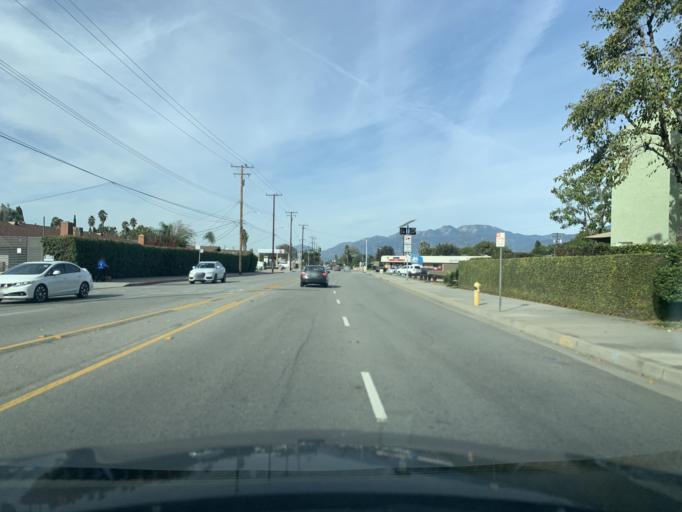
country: US
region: California
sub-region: Los Angeles County
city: West Covina
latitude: 34.0736
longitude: -117.9447
